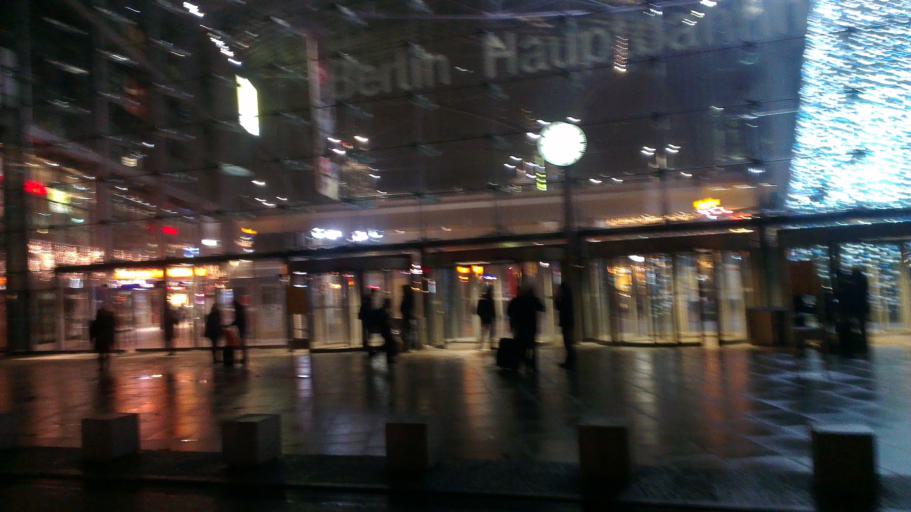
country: DE
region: Berlin
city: Tiergarten Bezirk
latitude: 52.5242
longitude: 13.3699
